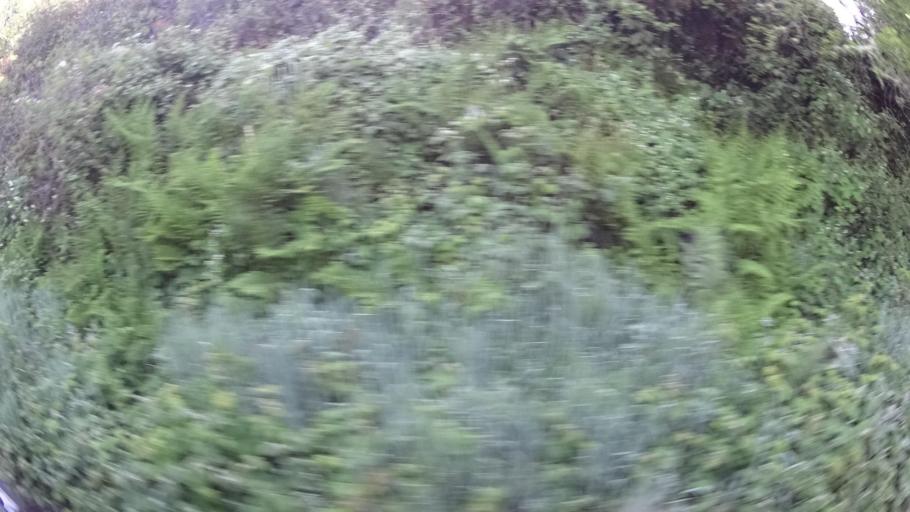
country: US
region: California
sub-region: Humboldt County
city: Westhaven-Moonstone
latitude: 41.1197
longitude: -124.1567
